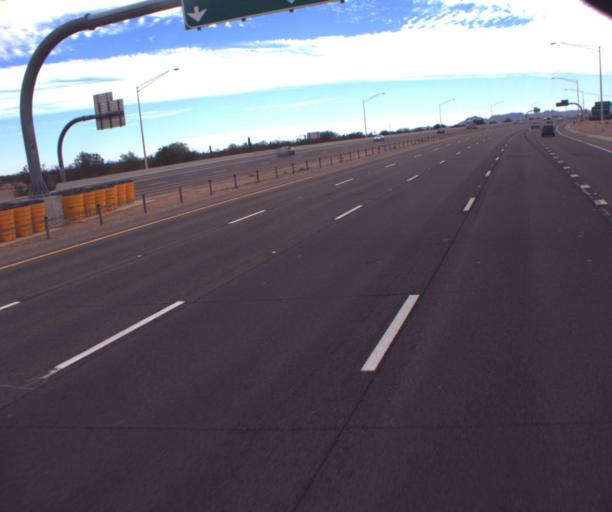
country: US
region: Arizona
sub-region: Maricopa County
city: Queen Creek
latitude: 33.3437
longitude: -111.6440
